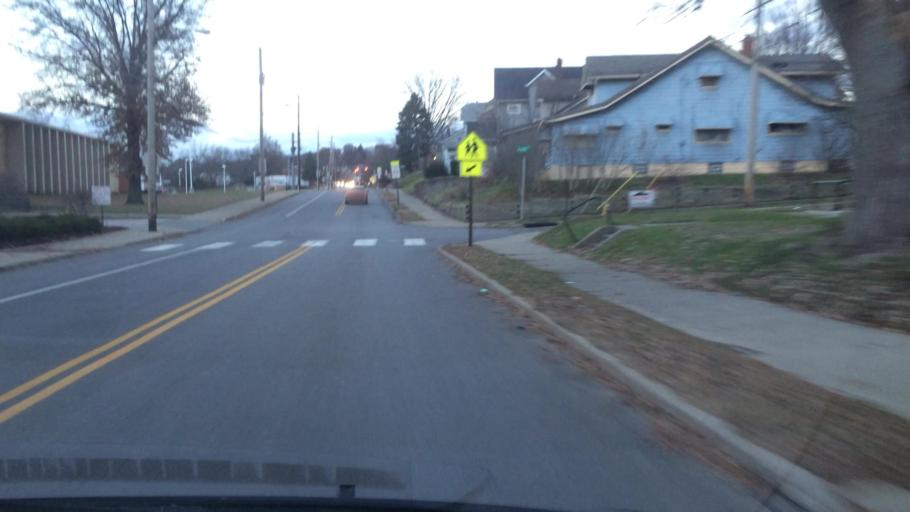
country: US
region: Ohio
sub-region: Summit County
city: Sawyerwood
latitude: 41.0634
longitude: -81.4668
